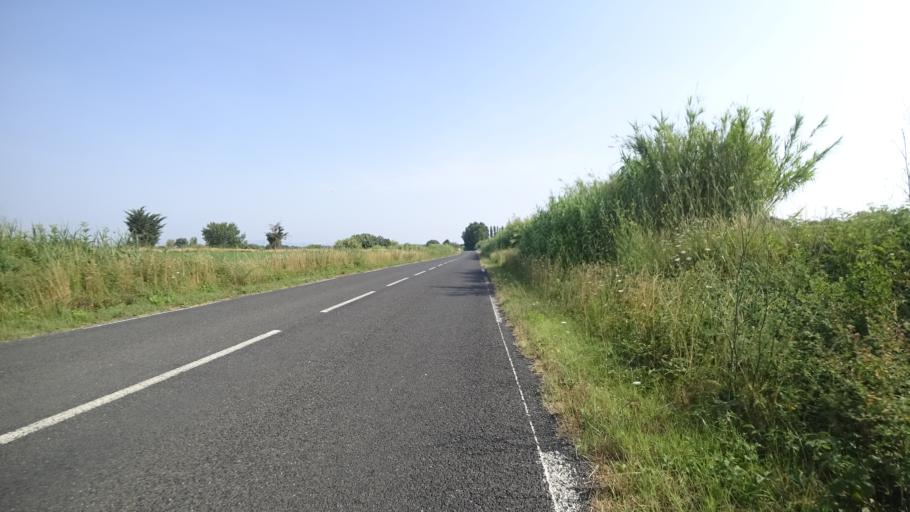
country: FR
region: Languedoc-Roussillon
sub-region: Departement des Pyrenees-Orientales
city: Villelongue-de-la-Salanque
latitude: 42.7378
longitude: 2.9894
